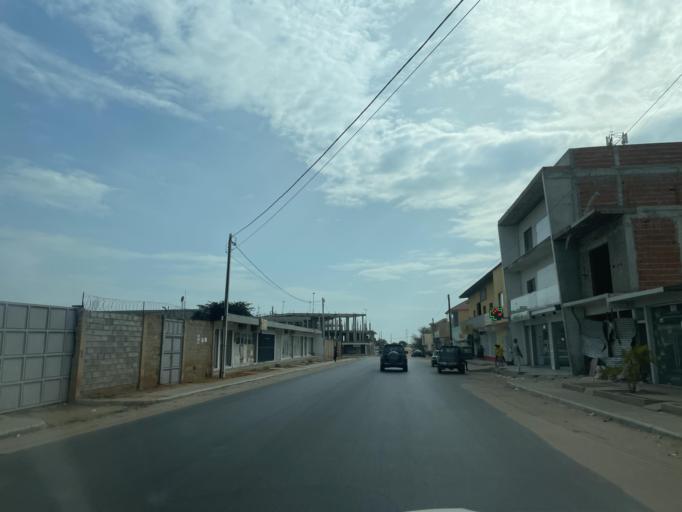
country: AO
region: Luanda
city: Luanda
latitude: -8.9418
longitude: 13.1920
